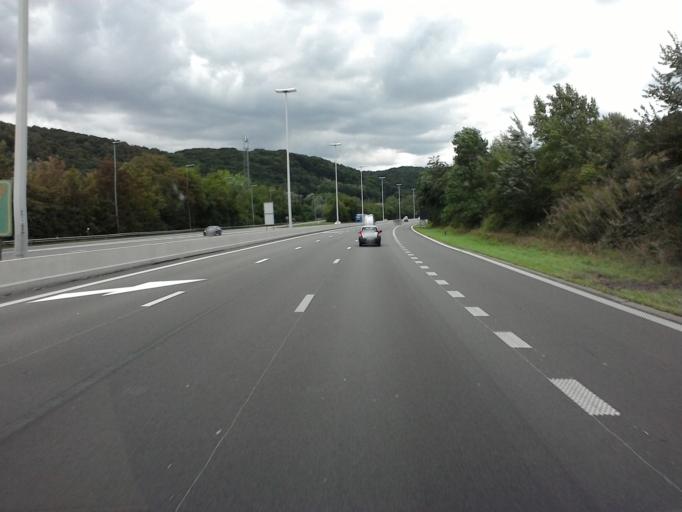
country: BE
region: Wallonia
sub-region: Province de Liege
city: Chaudfontaine
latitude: 50.5897
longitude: 5.5918
